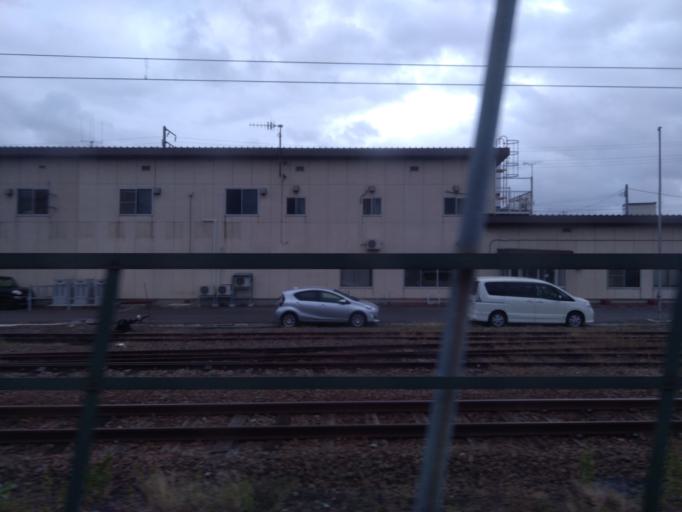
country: JP
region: Hokkaido
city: Hakodate
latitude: 41.8044
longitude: 140.7334
